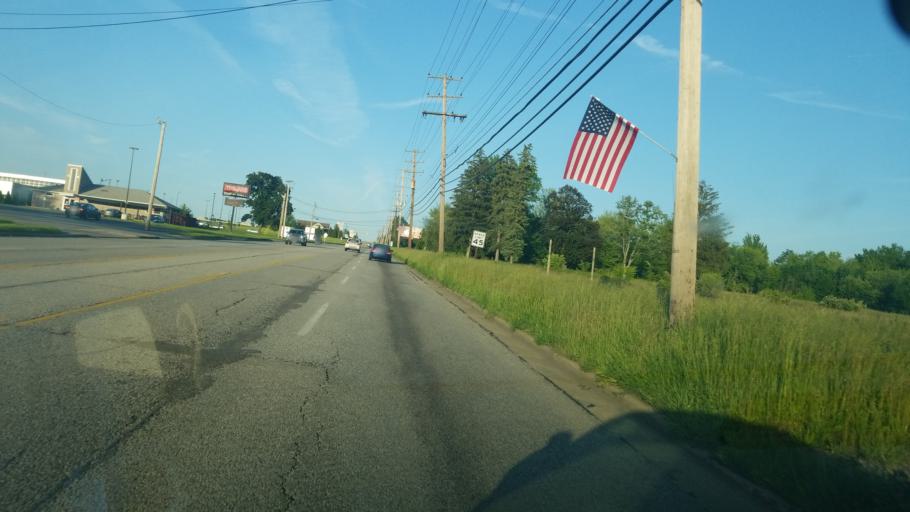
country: US
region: Ohio
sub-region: Mahoning County
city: Austintown
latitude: 41.0995
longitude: -80.7840
